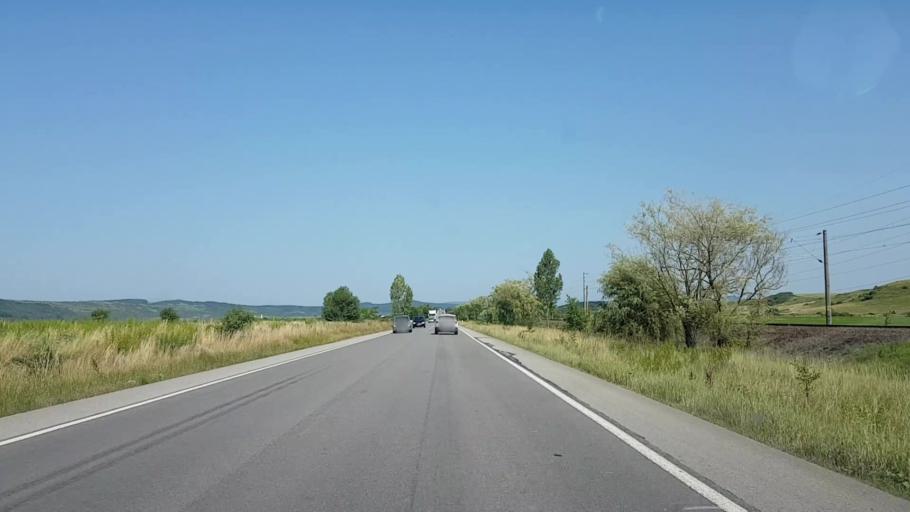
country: RO
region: Bistrita-Nasaud
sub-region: Comuna Sintereag
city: Cociu
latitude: 47.1836
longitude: 24.2182
